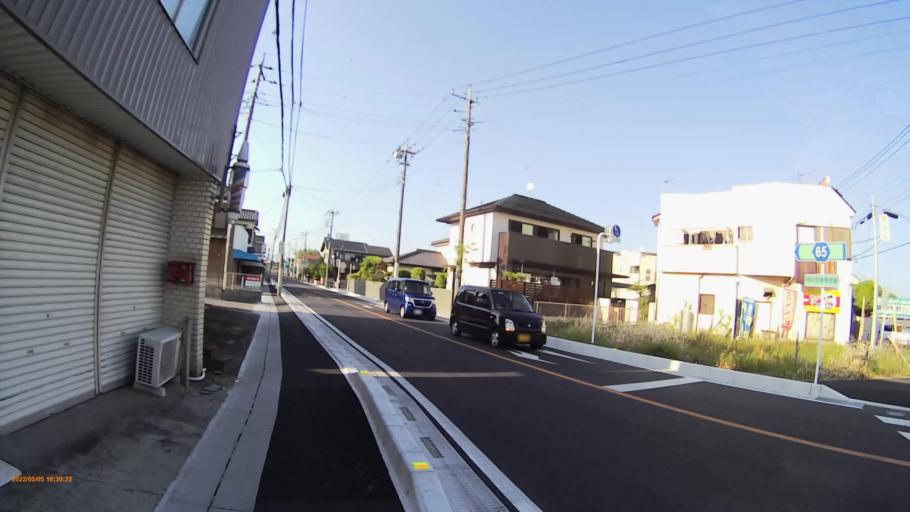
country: JP
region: Saitama
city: Satte
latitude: 36.0816
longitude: 139.7217
